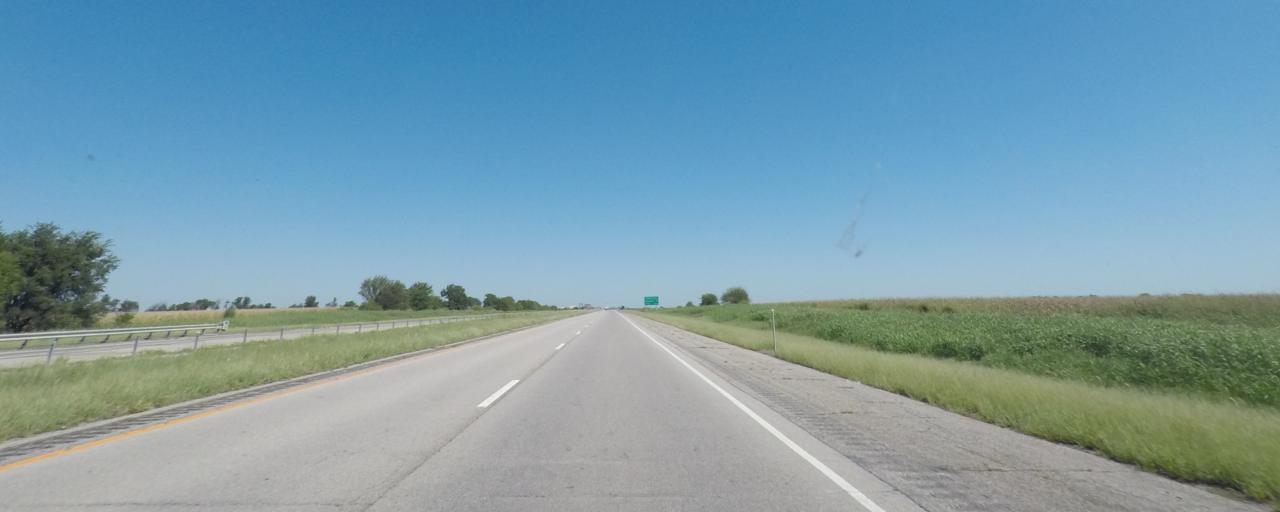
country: US
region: Oklahoma
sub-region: Kay County
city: Tonkawa
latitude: 36.7275
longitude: -97.3457
